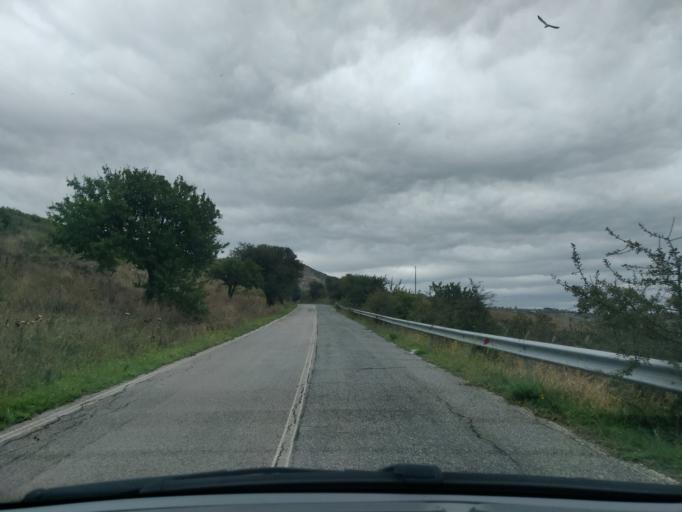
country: IT
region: Latium
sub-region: Citta metropolitana di Roma Capitale
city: Aurelia
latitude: 42.1310
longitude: 11.8424
